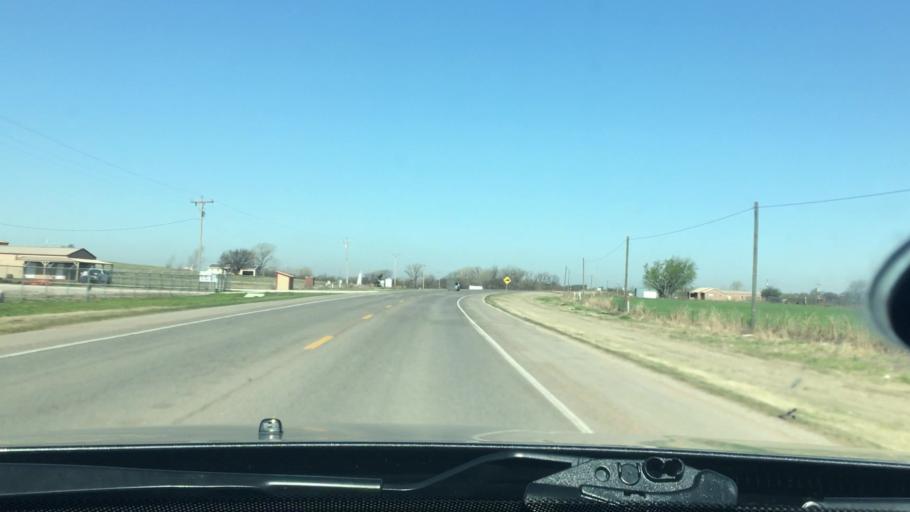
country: US
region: Oklahoma
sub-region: Garvin County
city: Lindsay
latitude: 34.8282
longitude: -97.5650
